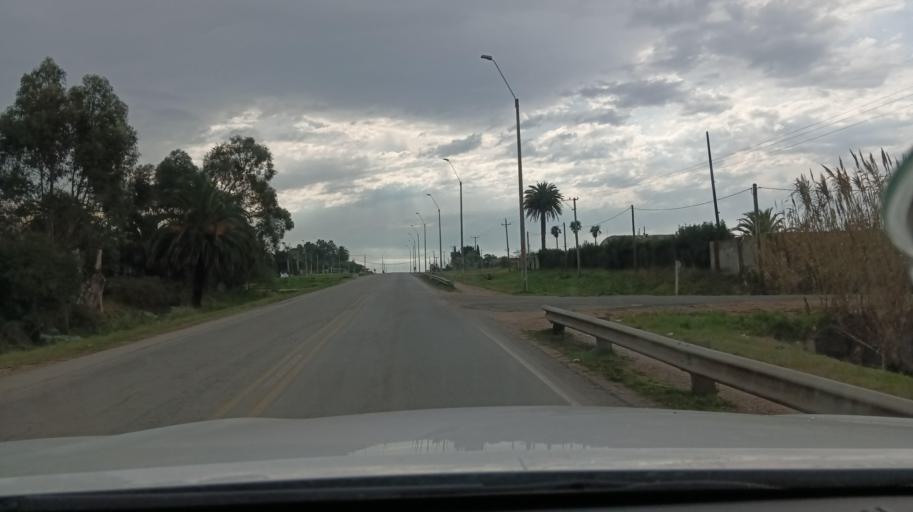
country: UY
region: Canelones
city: Toledo
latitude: -34.7498
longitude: -56.1094
